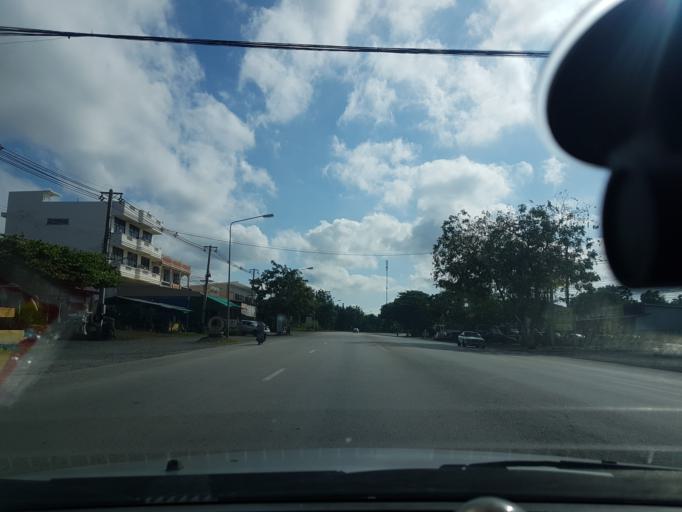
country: TH
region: Lop Buri
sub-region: Amphoe Tha Luang
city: Tha Luang
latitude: 15.0795
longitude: 101.0468
